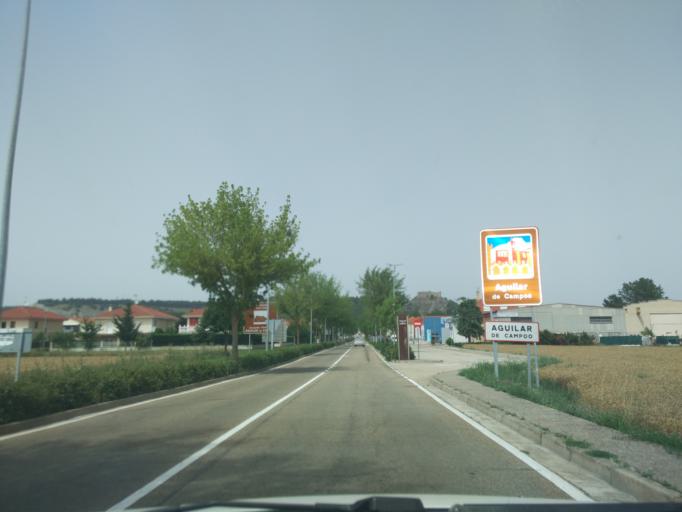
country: ES
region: Castille and Leon
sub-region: Provincia de Palencia
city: Aguilar de Campoo
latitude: 42.7867
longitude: -4.2668
